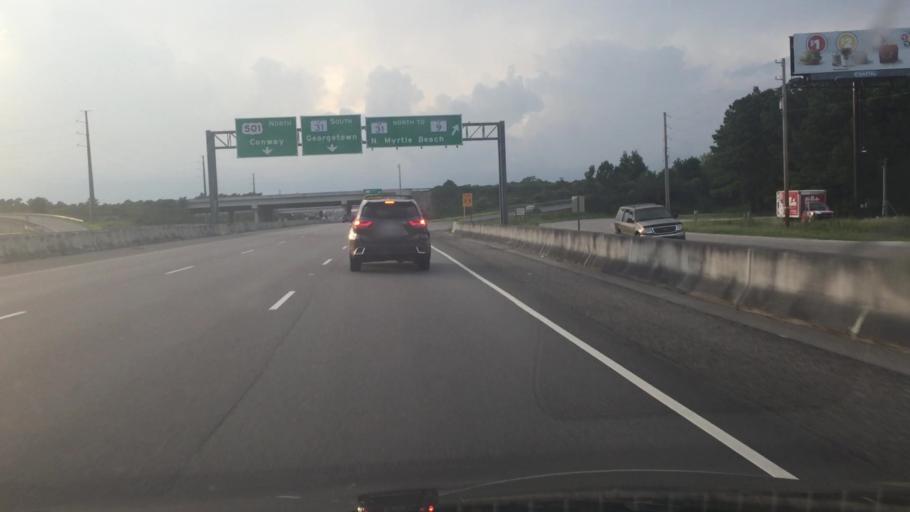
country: US
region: South Carolina
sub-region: Horry County
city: Forestbrook
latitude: 33.7374
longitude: -78.9486
